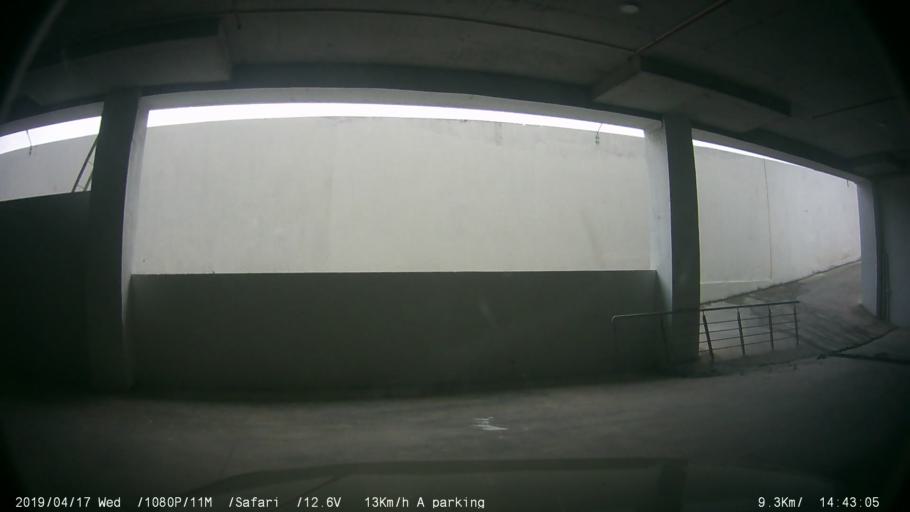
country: IN
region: Karnataka
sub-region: Bangalore Urban
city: Anekal
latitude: 12.8404
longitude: 77.6539
